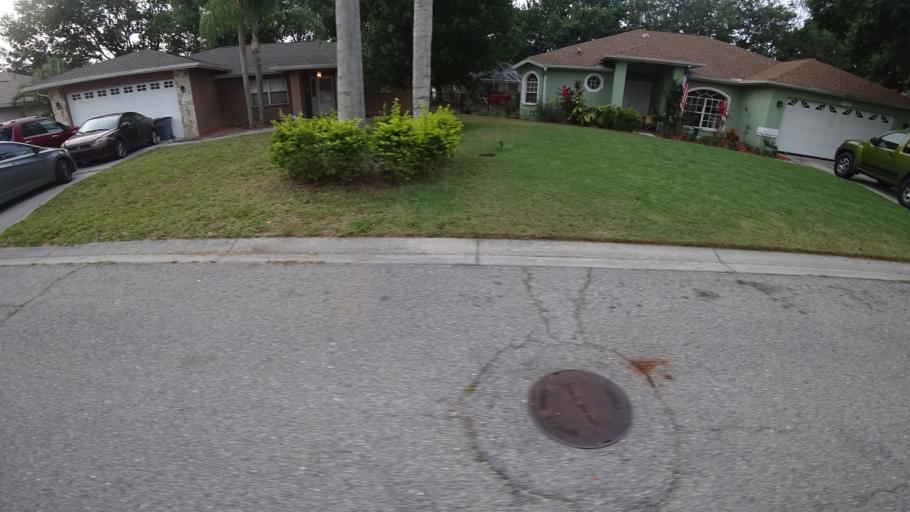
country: US
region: Florida
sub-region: Manatee County
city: Samoset
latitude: 27.4382
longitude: -82.5284
